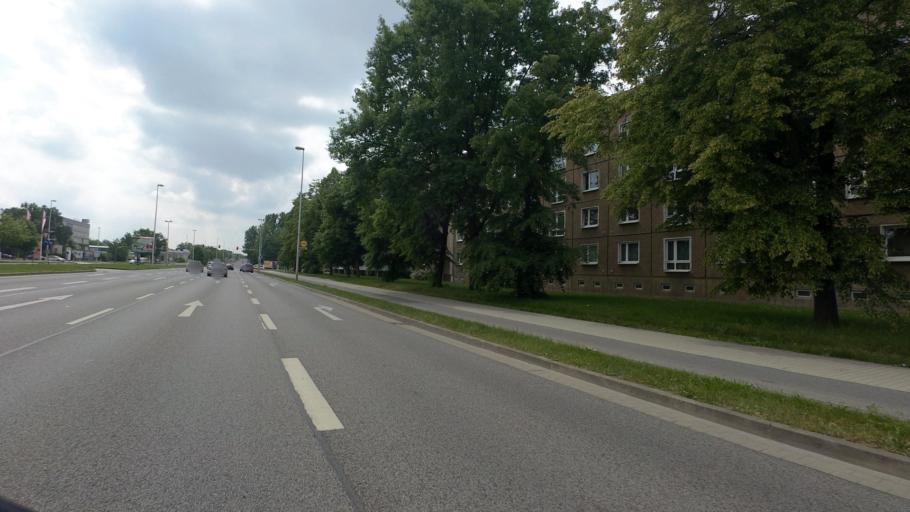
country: DE
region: Brandenburg
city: Cottbus
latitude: 51.7637
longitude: 14.3585
